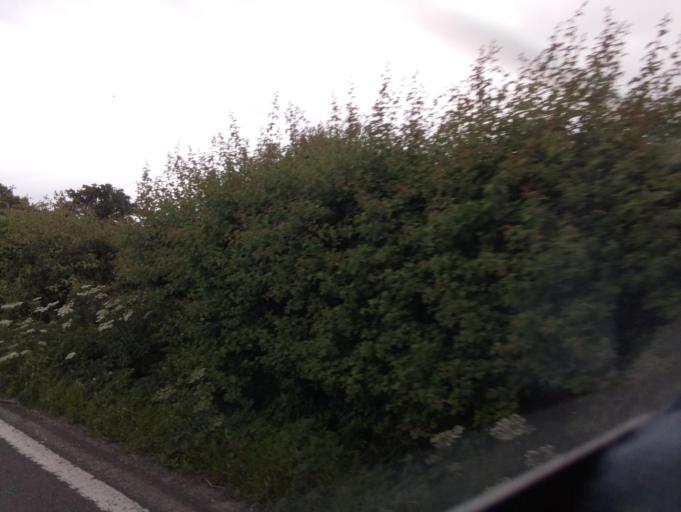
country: GB
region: England
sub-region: Staffordshire
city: Mayfield
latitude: 52.9426
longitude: -1.7604
